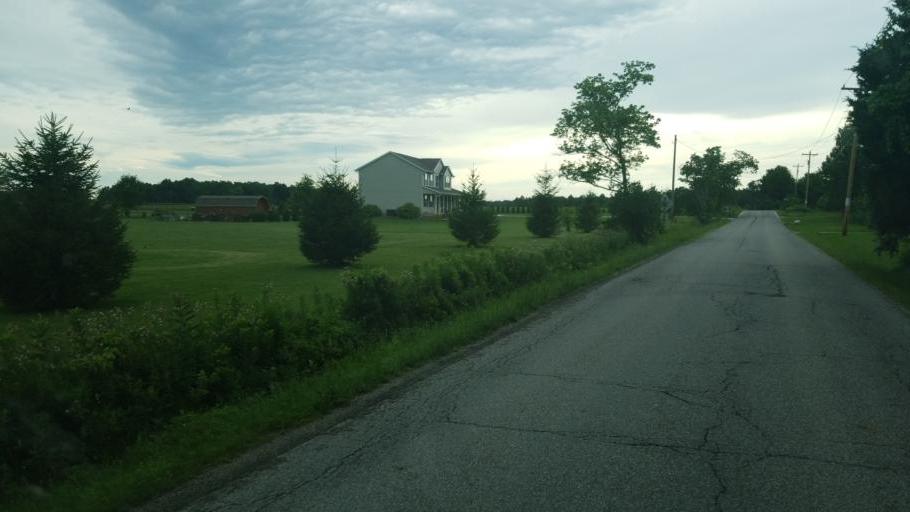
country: US
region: Ohio
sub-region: Delaware County
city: Ashley
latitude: 40.3622
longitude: -82.9278
